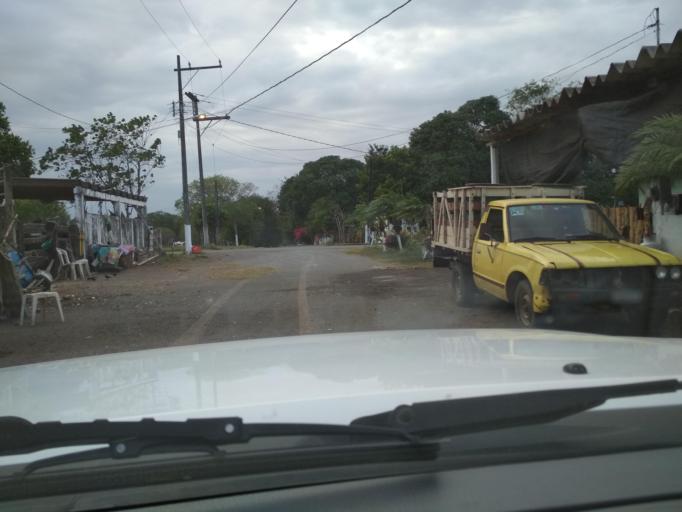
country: MX
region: Veracruz
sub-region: Veracruz
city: Delfino Victoria (Santa Fe)
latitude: 19.1585
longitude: -96.2937
